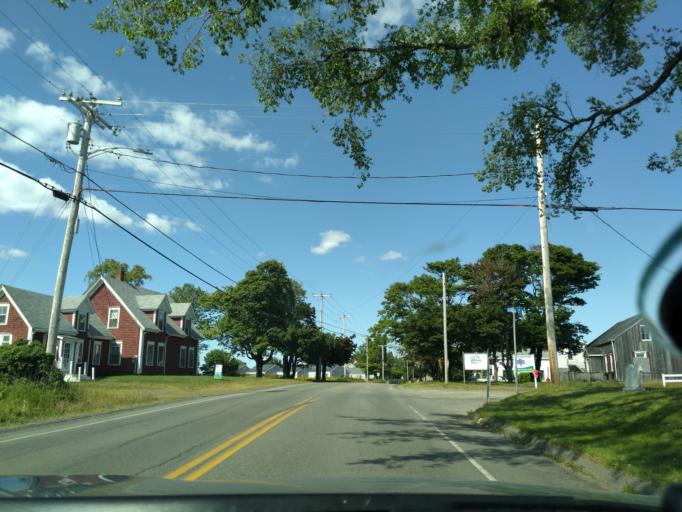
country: US
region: Maine
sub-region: Washington County
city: Eastport
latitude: 44.8558
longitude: -66.9924
